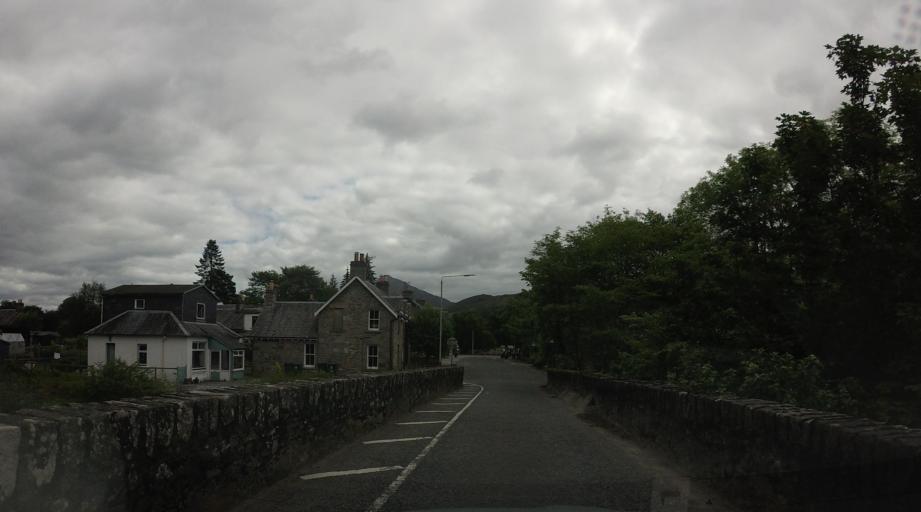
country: GB
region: Scotland
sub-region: Perth and Kinross
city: Aberfeldy
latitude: 56.6999
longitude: -4.1866
